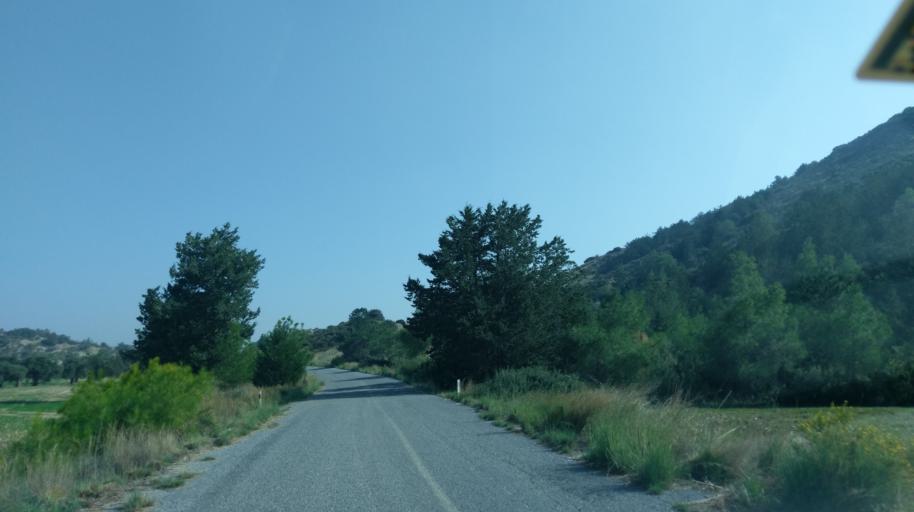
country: CY
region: Ammochostos
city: Lefkonoiko
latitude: 35.3198
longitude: 33.6620
